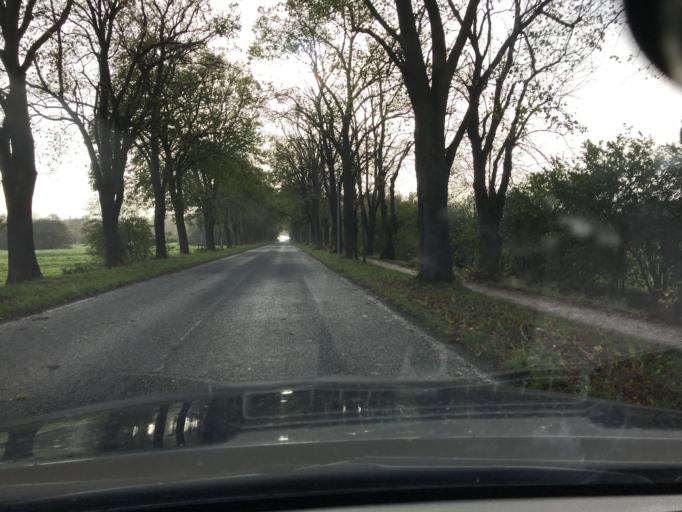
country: DE
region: Lower Saxony
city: Syke
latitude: 52.9448
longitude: 8.8203
